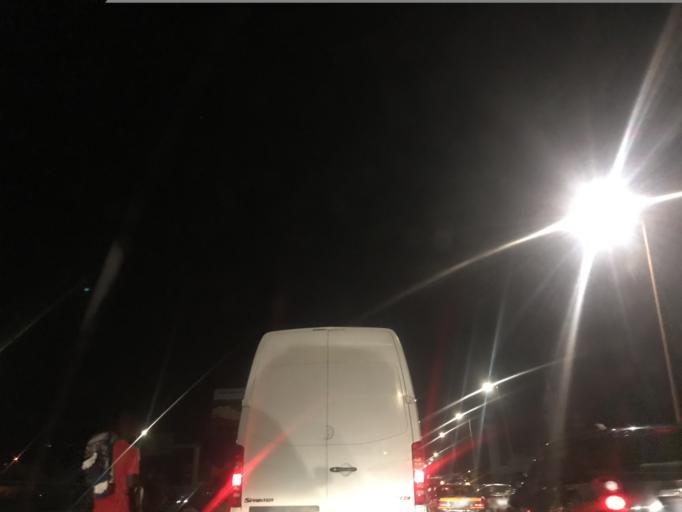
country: SN
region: Dakar
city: Grand Dakar
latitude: 14.7422
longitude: -17.4399
